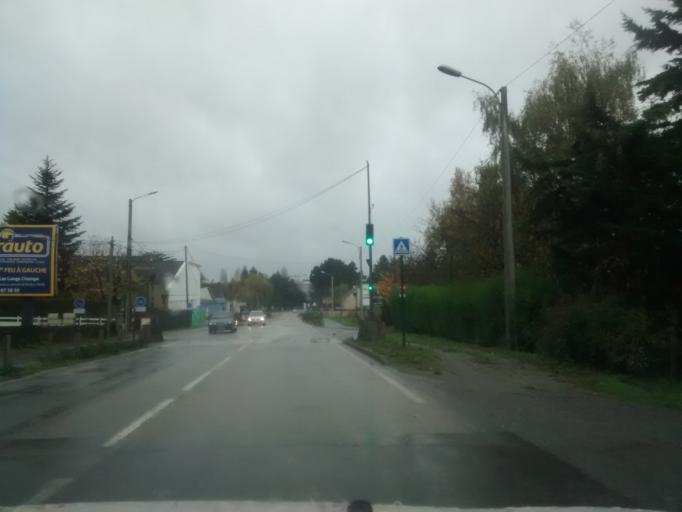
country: FR
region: Brittany
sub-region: Departement d'Ille-et-Vilaine
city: Cesson-Sevigne
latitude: 48.1348
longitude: -1.6275
